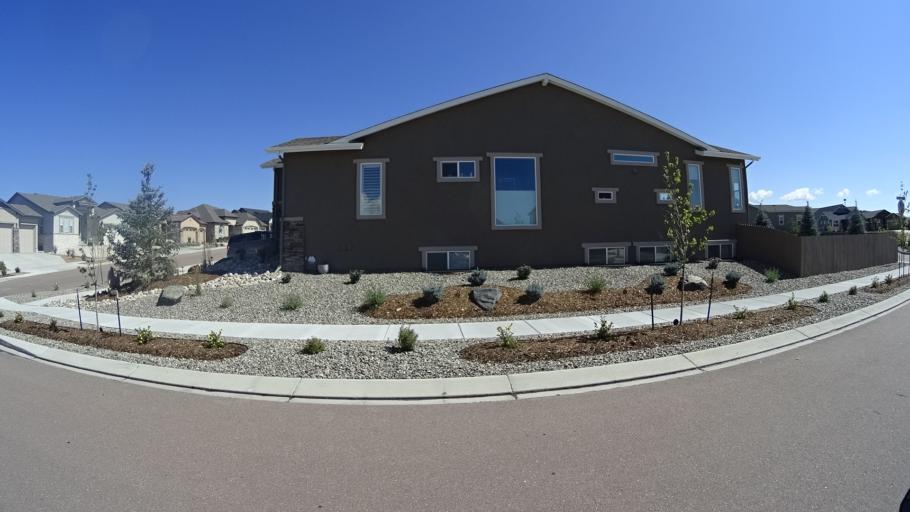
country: US
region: Colorado
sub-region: El Paso County
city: Black Forest
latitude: 38.9795
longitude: -104.7482
